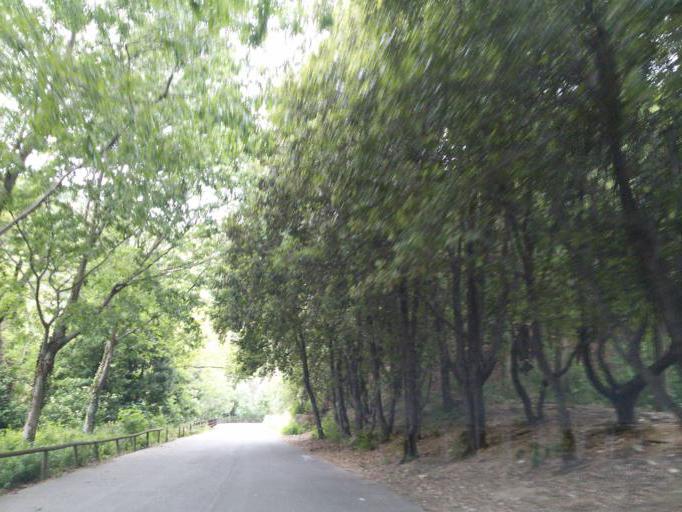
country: IT
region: Liguria
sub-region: Provincia di Genova
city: Genoa
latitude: 44.4305
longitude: 8.9273
